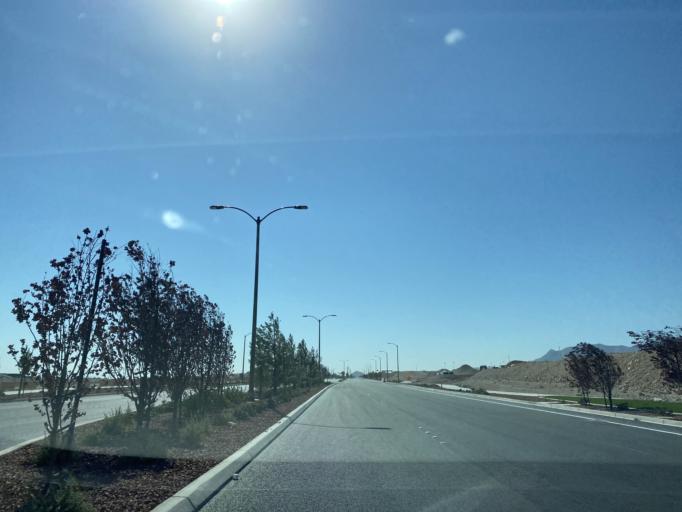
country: US
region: Nevada
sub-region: Clark County
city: Summerlin South
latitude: 36.3204
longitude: -115.3149
